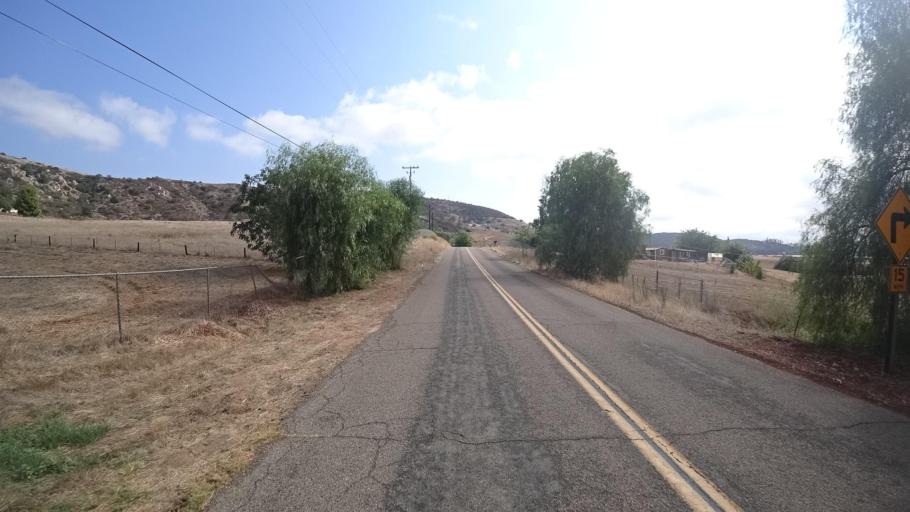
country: US
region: California
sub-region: San Diego County
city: Ramona
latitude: 33.0268
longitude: -116.8372
